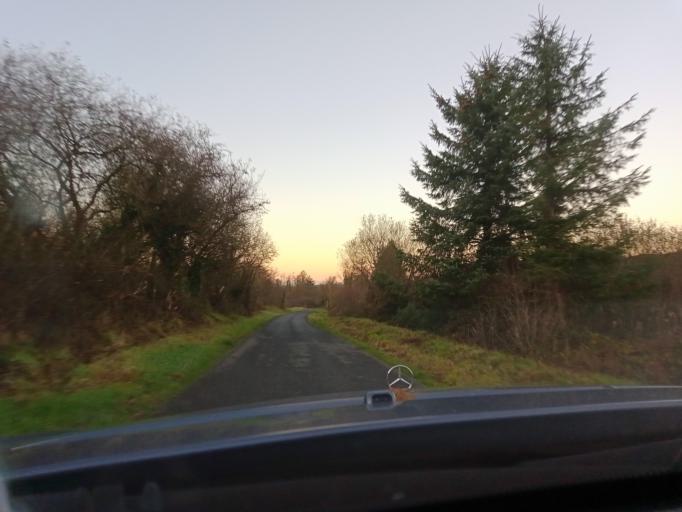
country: IE
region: Leinster
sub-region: Kilkenny
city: Thomastown
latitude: 52.4361
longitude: -7.1083
